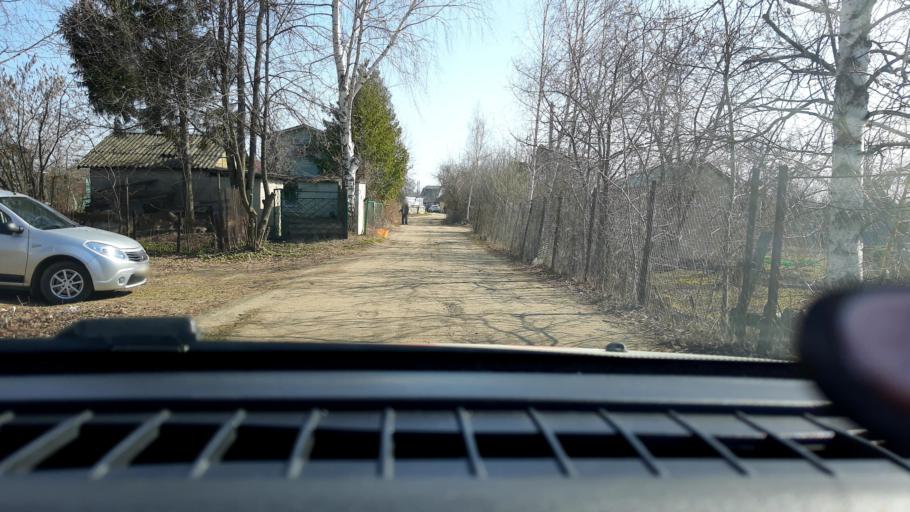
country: RU
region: Nizjnij Novgorod
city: Gorbatovka
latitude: 56.2637
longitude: 43.8232
